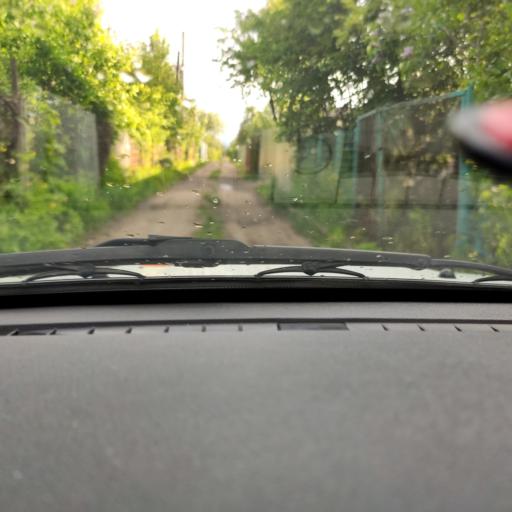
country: RU
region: Voronezj
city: Shilovo
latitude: 51.5872
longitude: 39.1601
